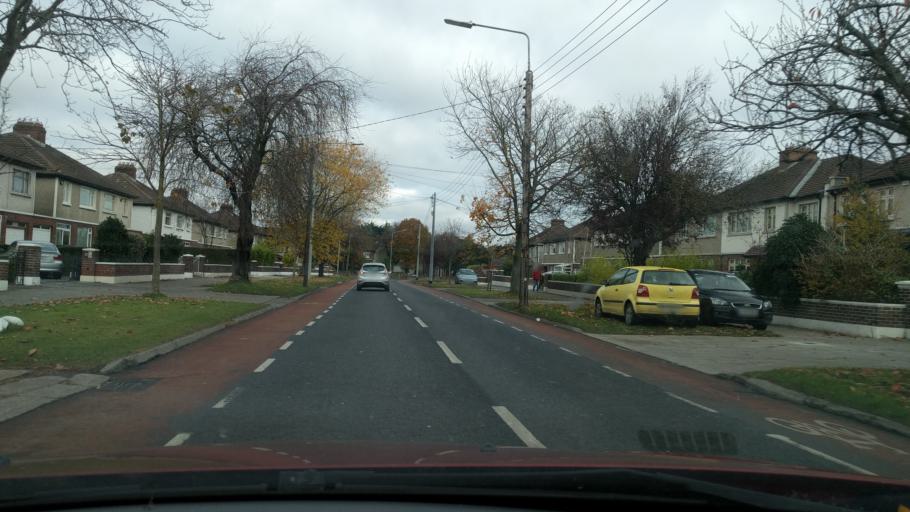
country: IE
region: Leinster
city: Templeogue
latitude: 53.3078
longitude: -6.3057
